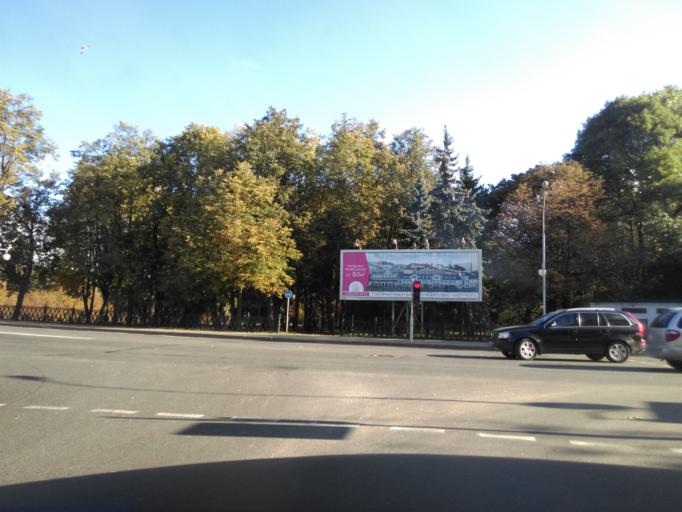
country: BY
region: Minsk
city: Minsk
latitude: 53.9060
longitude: 27.5639
